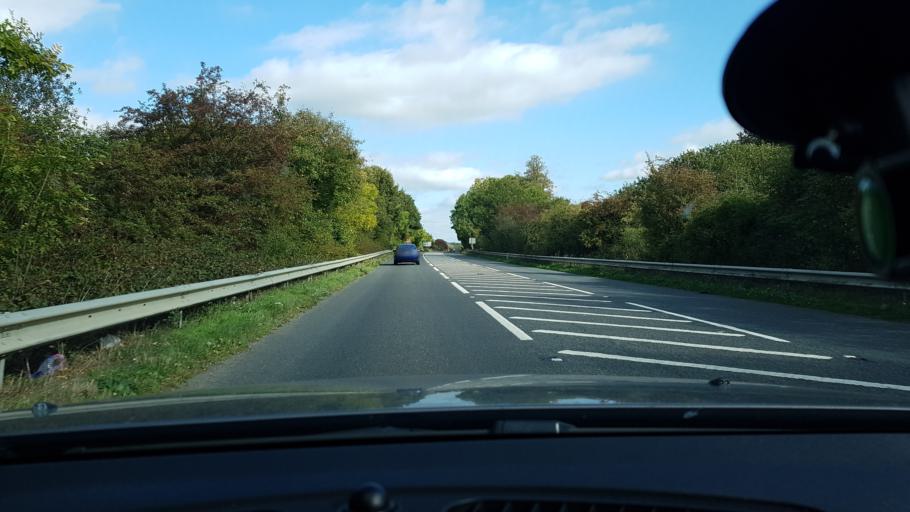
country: GB
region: England
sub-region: West Berkshire
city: Kintbury
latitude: 51.4132
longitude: -1.4525
